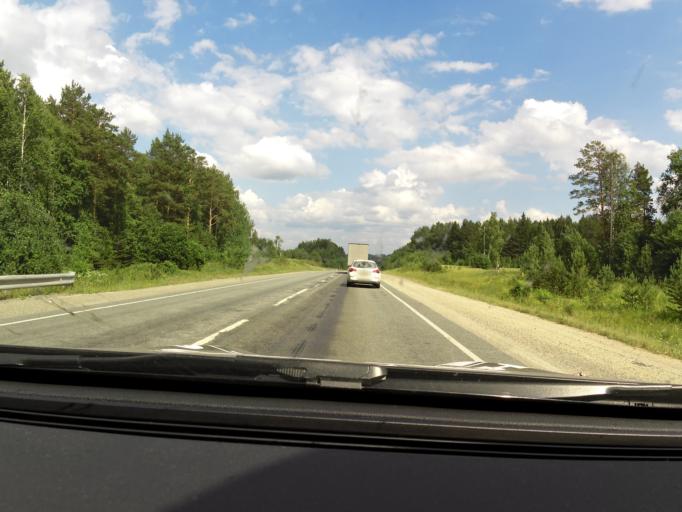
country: RU
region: Sverdlovsk
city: Bisert'
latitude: 56.8292
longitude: 59.0216
